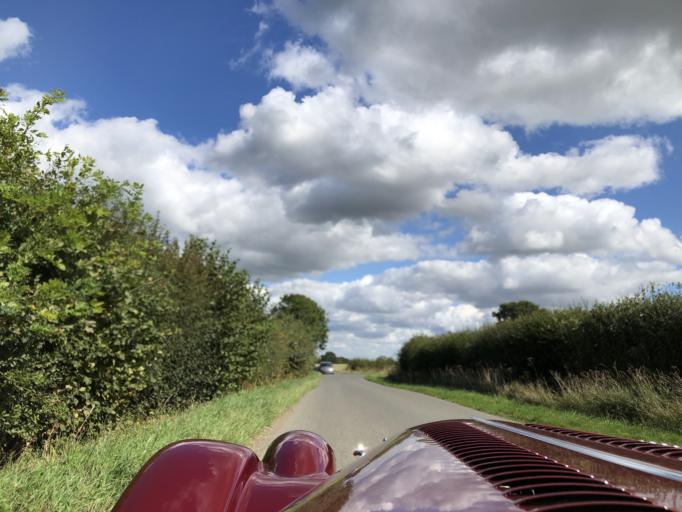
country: GB
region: England
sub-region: East Sussex
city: Northiam
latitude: 50.9942
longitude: 0.5618
